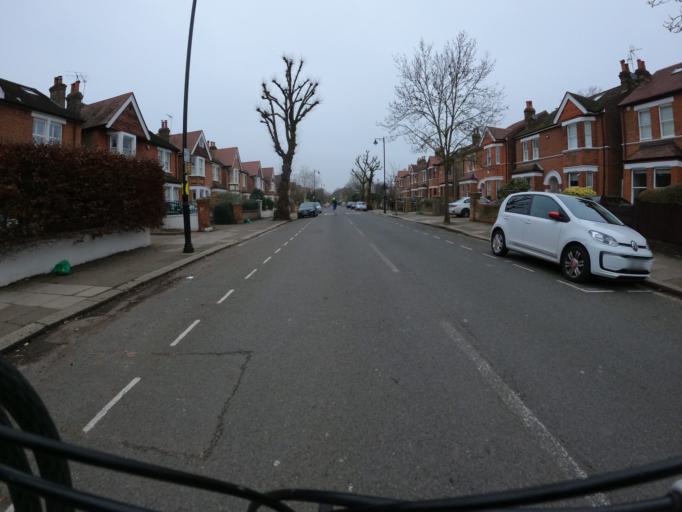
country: GB
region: England
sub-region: Greater London
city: Ealing
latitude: 51.5073
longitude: -0.3118
